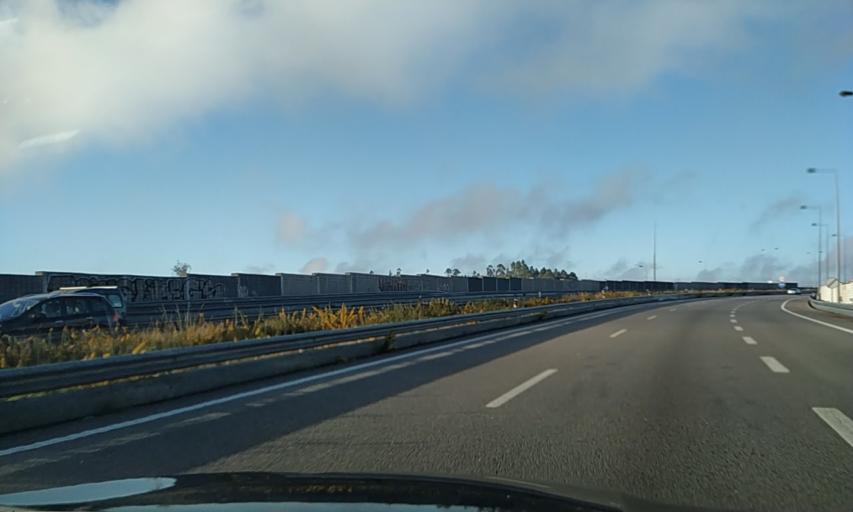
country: PT
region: Porto
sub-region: Pacos de Ferreira
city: Ferreira
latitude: 41.2614
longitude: -8.3342
